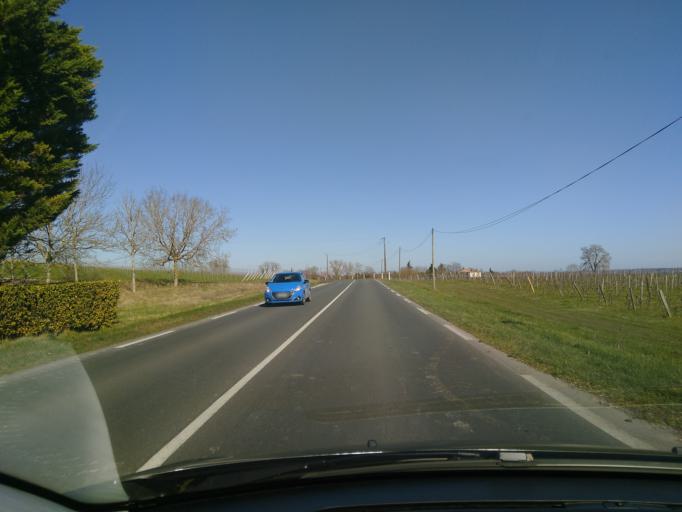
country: FR
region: Aquitaine
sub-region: Departement de la Dordogne
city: Monbazillac
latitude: 44.7649
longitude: 0.5274
